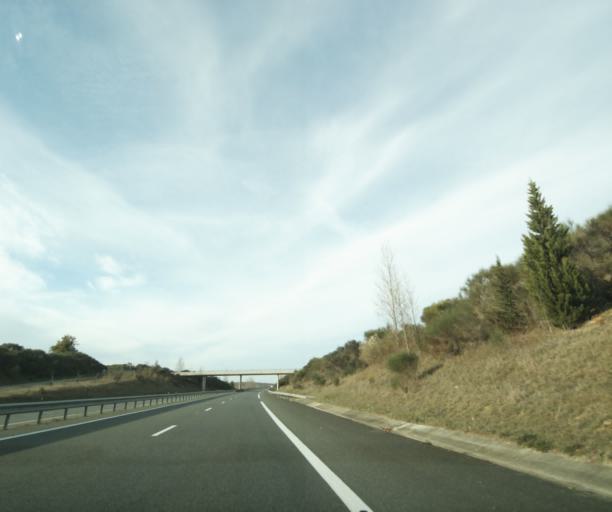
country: FR
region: Midi-Pyrenees
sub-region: Departement du Gers
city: Aubiet
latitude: 43.6469
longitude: 0.7978
